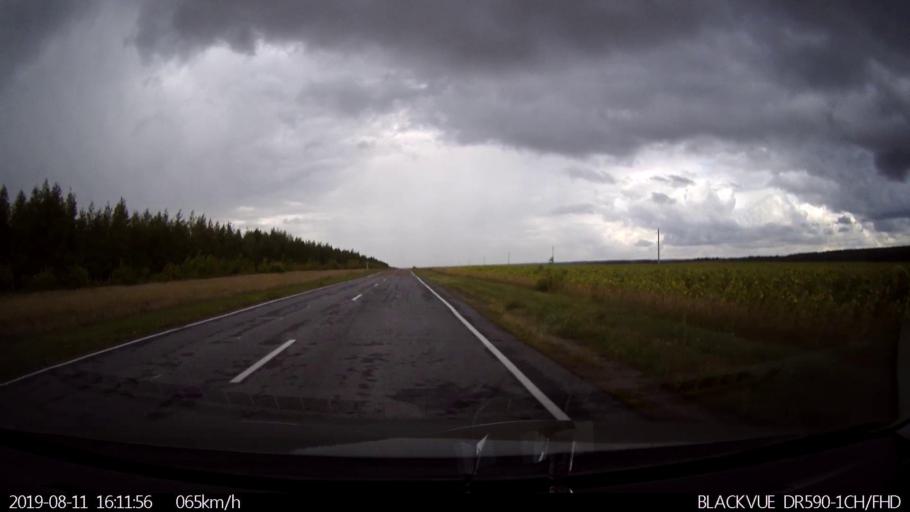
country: RU
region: Ulyanovsk
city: Ignatovka
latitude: 54.0070
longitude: 47.6422
